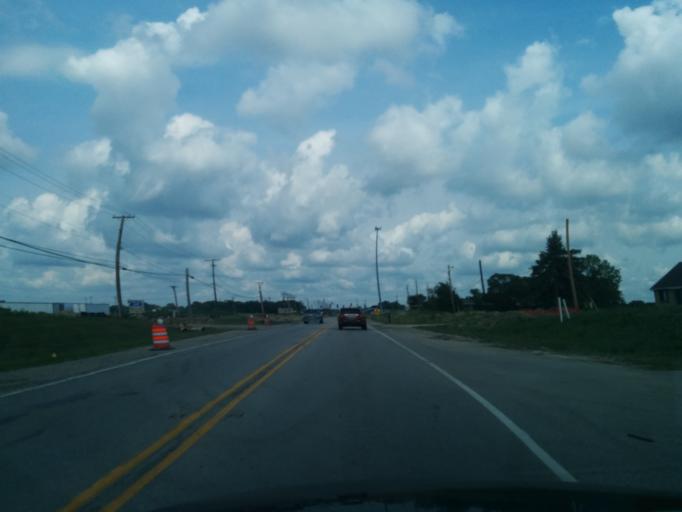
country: US
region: Illinois
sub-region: Will County
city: Homer Glen
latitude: 41.5995
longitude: -87.9532
